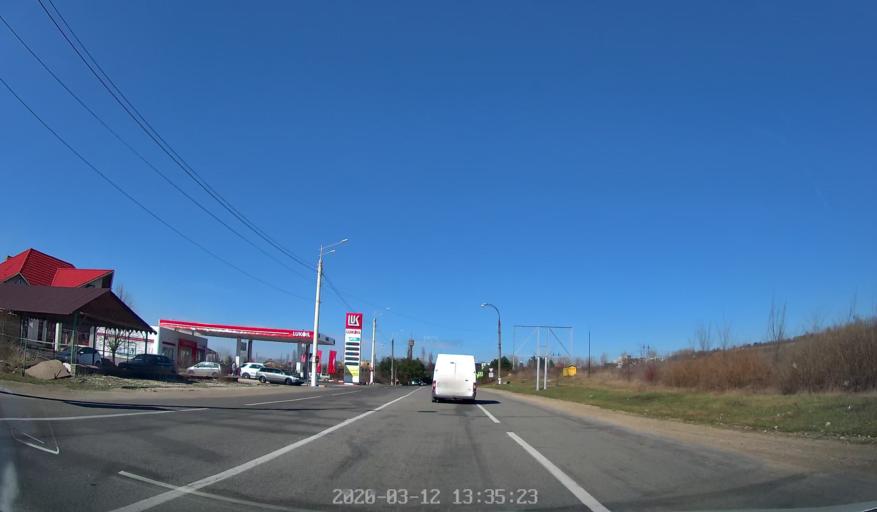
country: MD
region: Laloveni
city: Ialoveni
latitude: 46.9711
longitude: 28.7661
